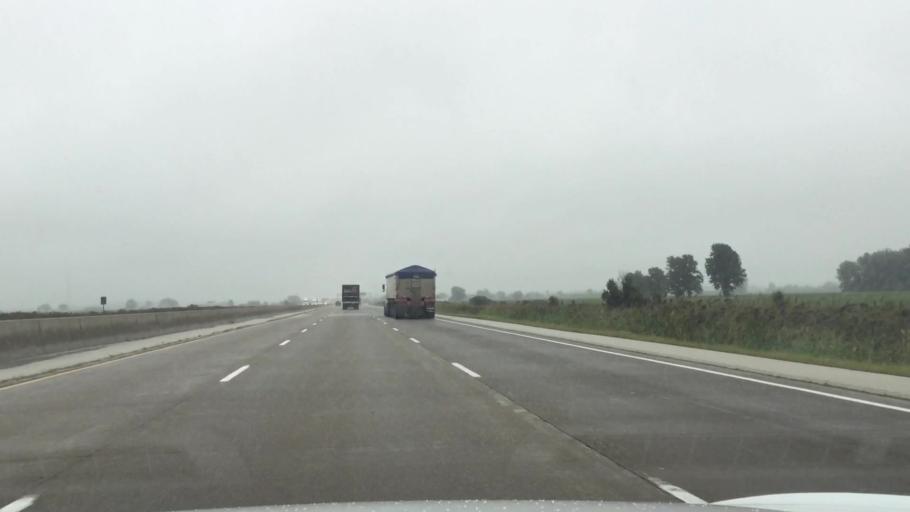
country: US
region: Michigan
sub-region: Wayne County
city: Grosse Pointe Farms
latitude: 42.2337
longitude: -82.6522
